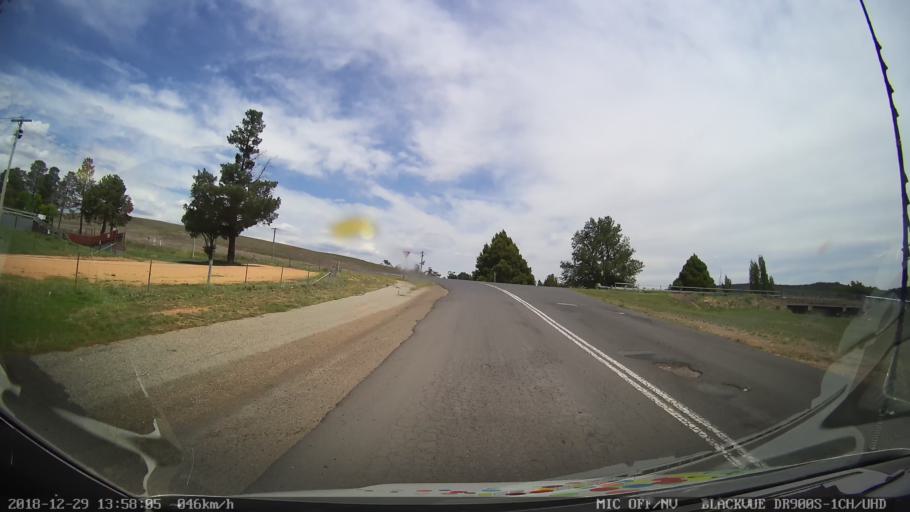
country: AU
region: New South Wales
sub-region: Cooma-Monaro
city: Cooma
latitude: -36.2431
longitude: 149.1372
